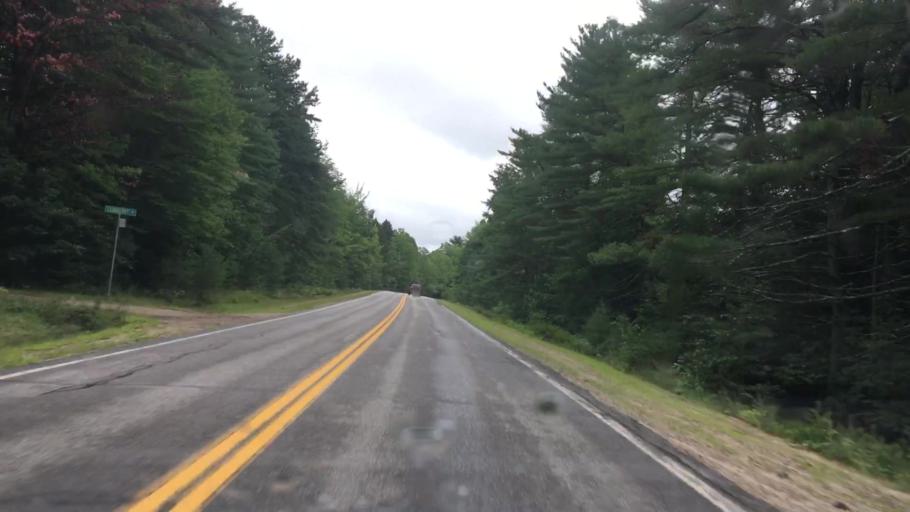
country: US
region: Maine
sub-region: Oxford County
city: Fryeburg
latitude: 43.9893
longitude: -70.9347
